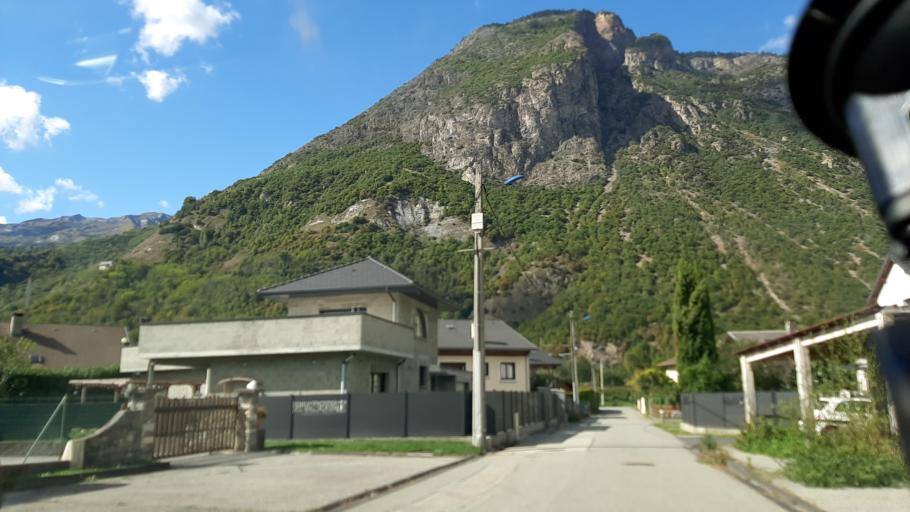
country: FR
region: Rhone-Alpes
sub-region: Departement de la Savoie
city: Saint-Jean-de-Maurienne
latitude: 45.2813
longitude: 6.3531
